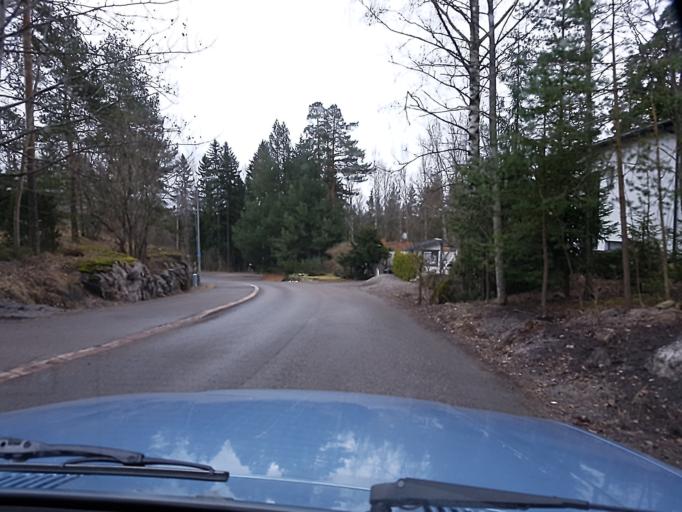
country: FI
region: Uusimaa
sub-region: Helsinki
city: Kauniainen
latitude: 60.2091
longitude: 24.6956
